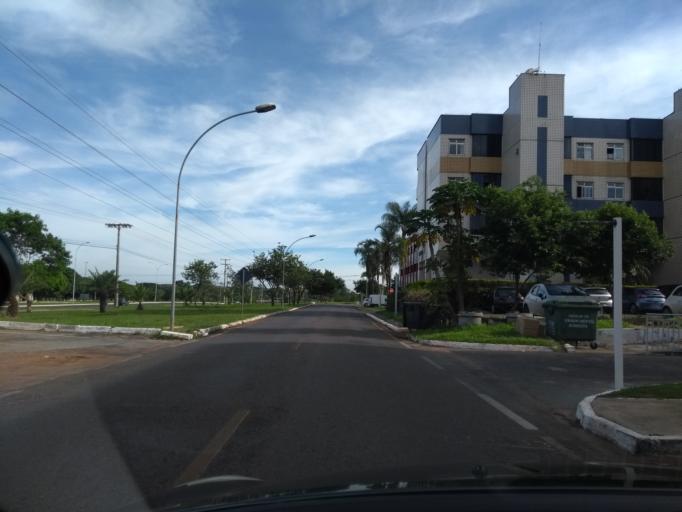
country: BR
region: Federal District
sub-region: Brasilia
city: Brasilia
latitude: -15.7836
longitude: -47.9300
